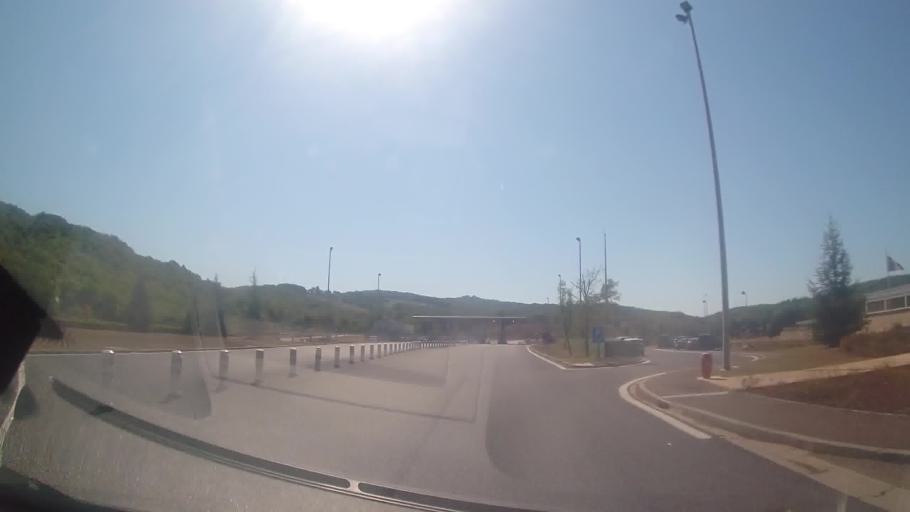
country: FR
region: Midi-Pyrenees
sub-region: Departement du Lot
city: Souillac
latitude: 44.9020
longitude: 1.5040
